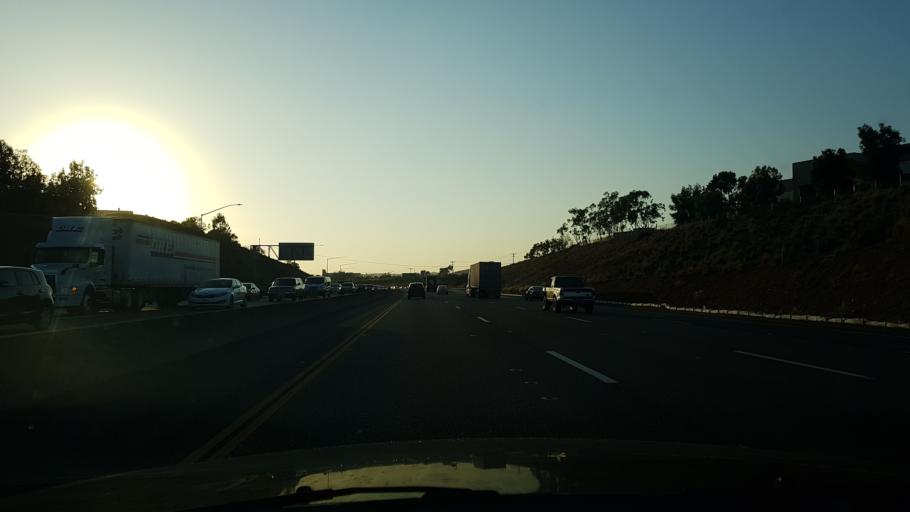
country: US
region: California
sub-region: San Diego County
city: San Marcos
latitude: 33.1395
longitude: -117.1474
